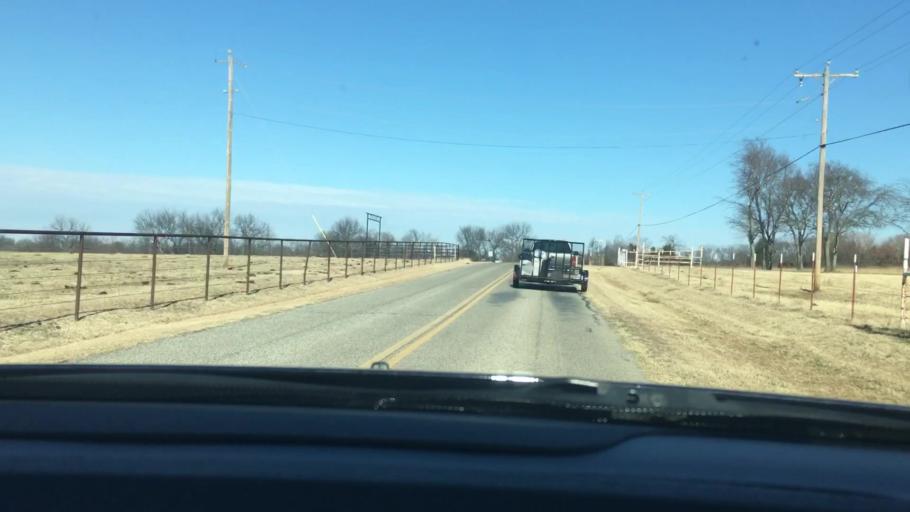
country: US
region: Oklahoma
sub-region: Murray County
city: Davis
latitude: 34.4818
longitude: -97.0556
